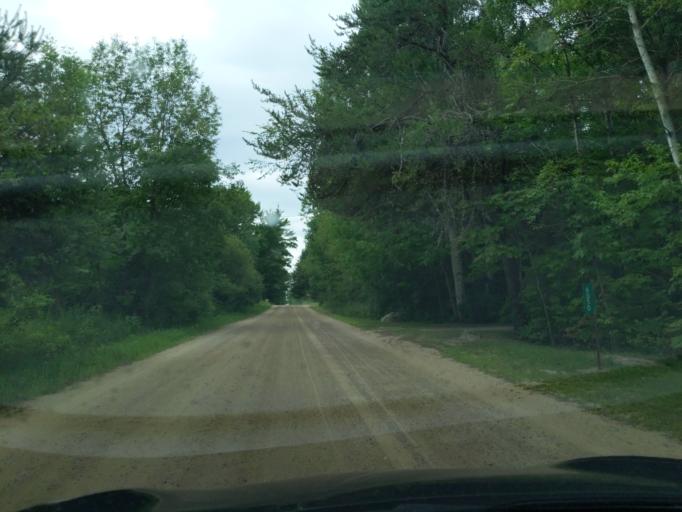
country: US
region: Michigan
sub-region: Clare County
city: Harrison
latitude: 44.0025
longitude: -84.9700
